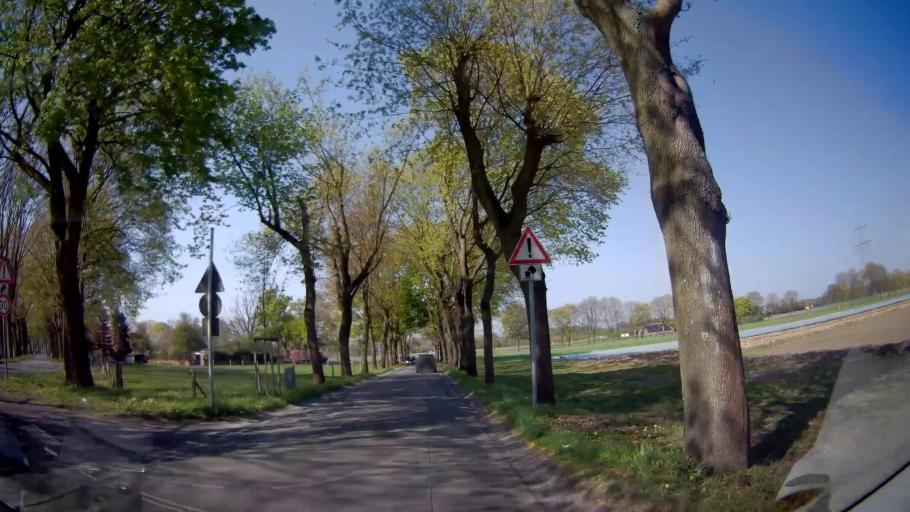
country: DE
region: North Rhine-Westphalia
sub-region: Regierungsbezirk Munster
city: Gladbeck
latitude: 51.5684
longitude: 7.0233
